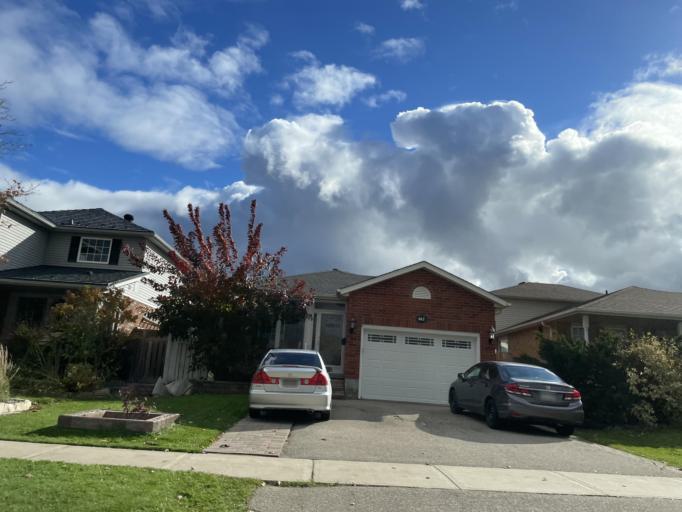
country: CA
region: Ontario
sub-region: Wellington County
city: Guelph
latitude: 43.5276
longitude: -80.2829
